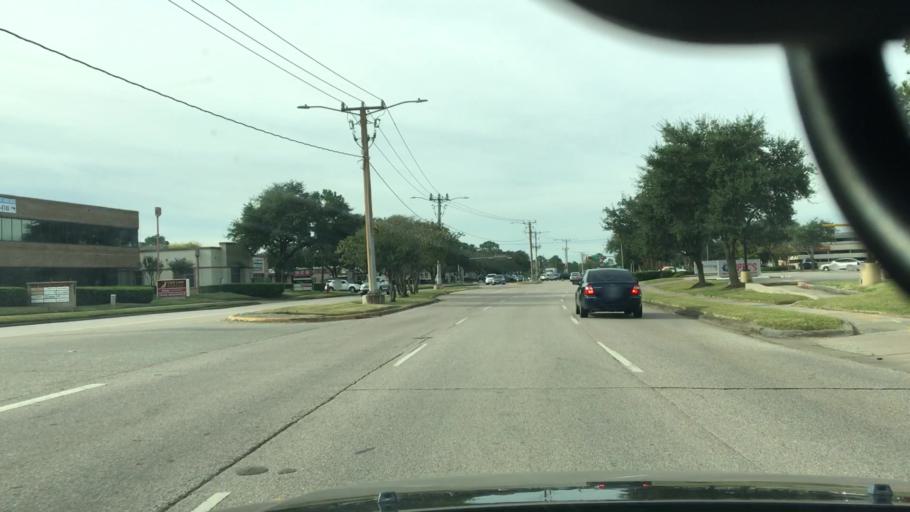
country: US
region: Texas
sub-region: Harris County
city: Webster
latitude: 29.5561
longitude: -95.1188
